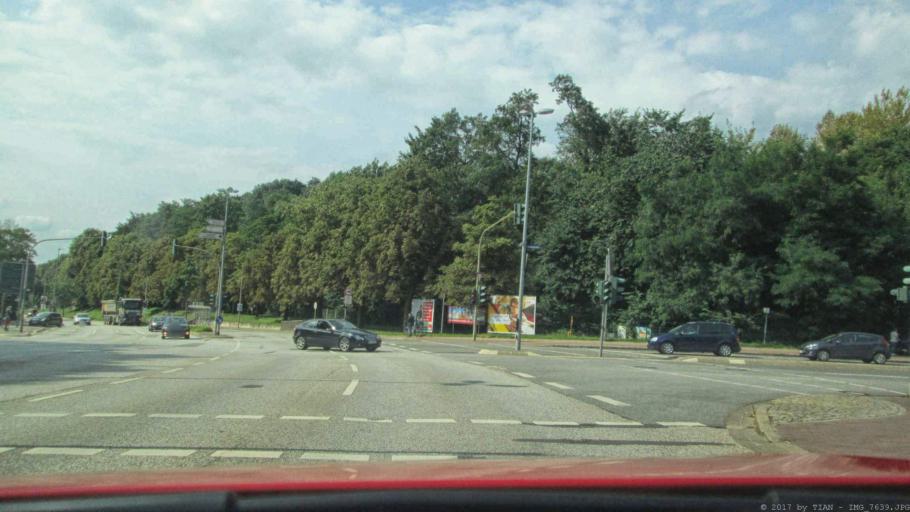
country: DE
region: Schleswig-Holstein
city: Geesthacht
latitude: 53.4357
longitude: 10.3860
